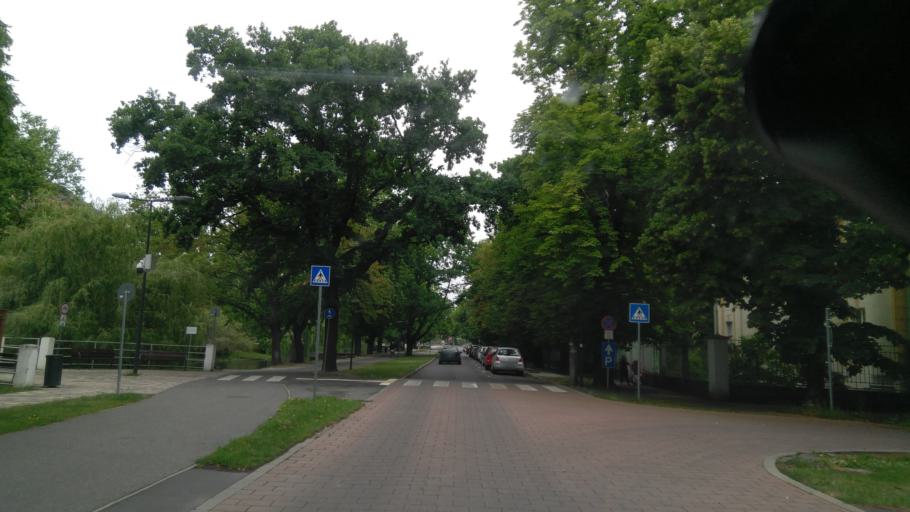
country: HU
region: Bekes
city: Bekescsaba
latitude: 46.6802
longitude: 21.1016
